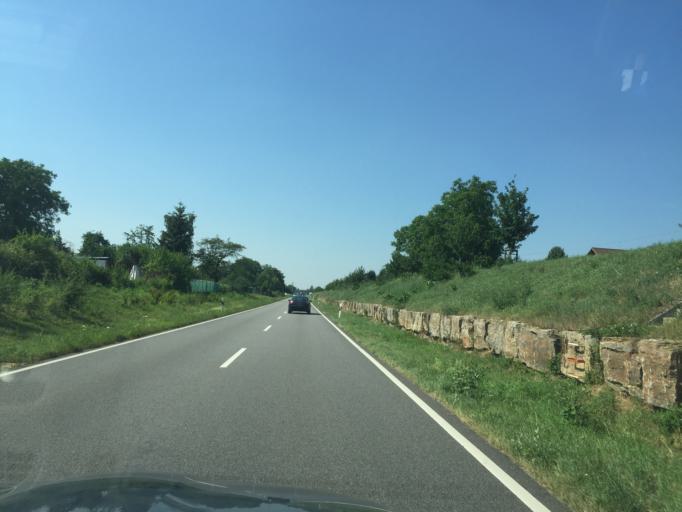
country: DE
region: Baden-Wuerttemberg
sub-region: Karlsruhe Region
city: Hemsbach
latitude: 49.5781
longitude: 8.6547
